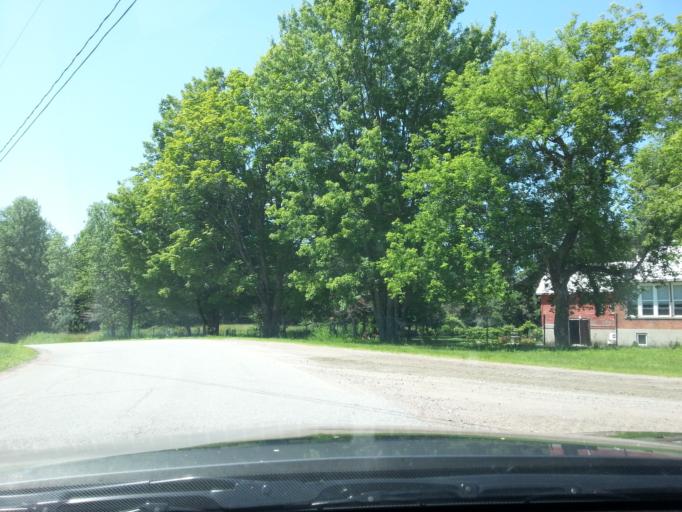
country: CA
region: Ontario
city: Arnprior
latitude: 45.5306
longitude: -76.3968
